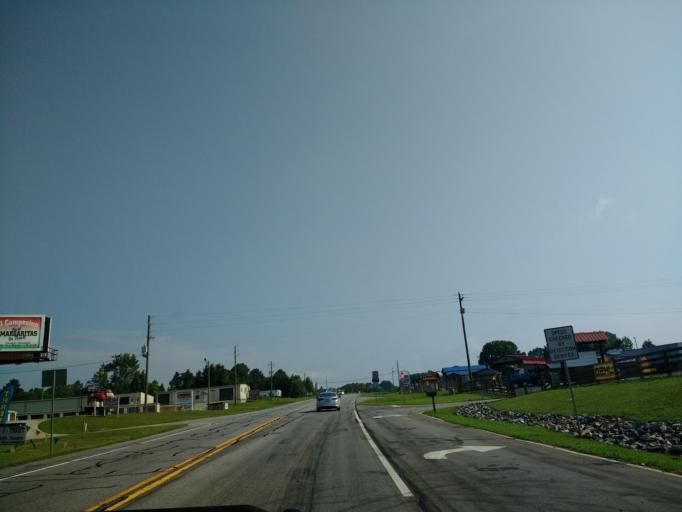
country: US
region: Georgia
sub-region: White County
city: Cleveland
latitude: 34.5047
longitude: -83.7567
